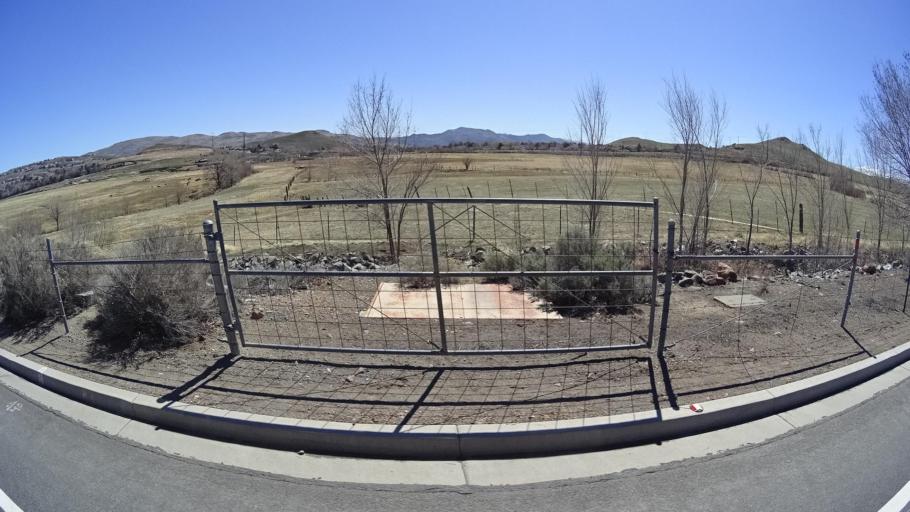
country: US
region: Nevada
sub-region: Washoe County
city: Sparks
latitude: 39.5751
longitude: -119.7324
